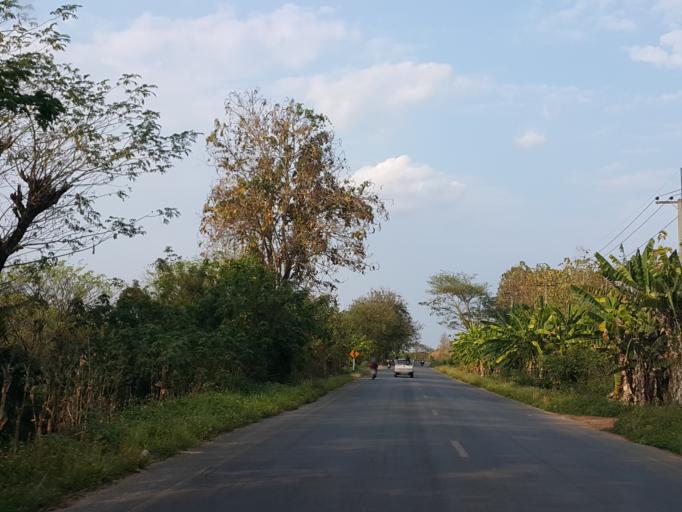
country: TH
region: Lampang
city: Hang Chat
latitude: 18.4454
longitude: 99.4513
